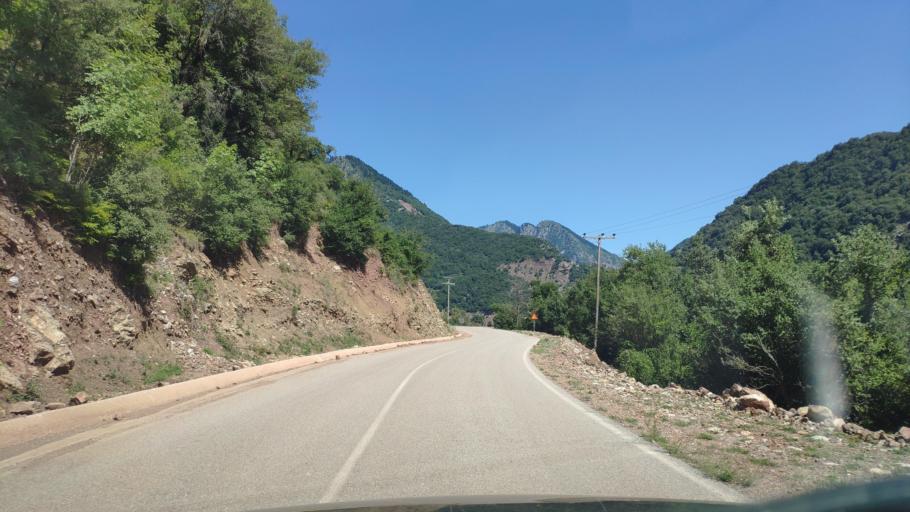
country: GR
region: Central Greece
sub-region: Nomos Evrytanias
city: Kerasochori
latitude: 39.0776
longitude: 21.5968
